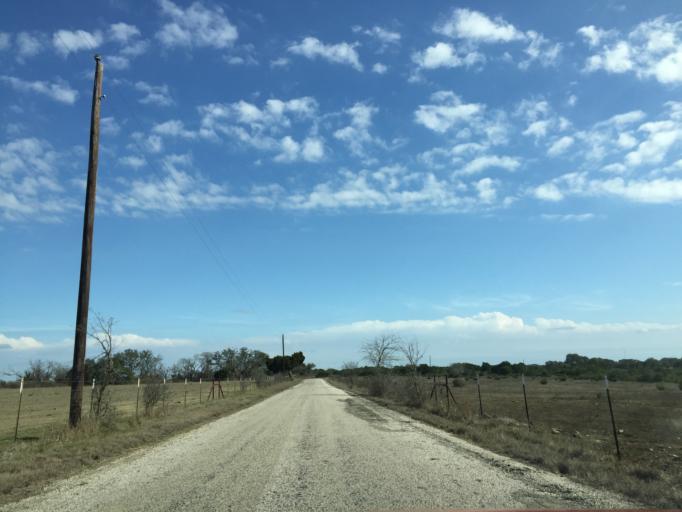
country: US
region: Texas
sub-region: Williamson County
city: Florence
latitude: 30.7813
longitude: -97.8933
